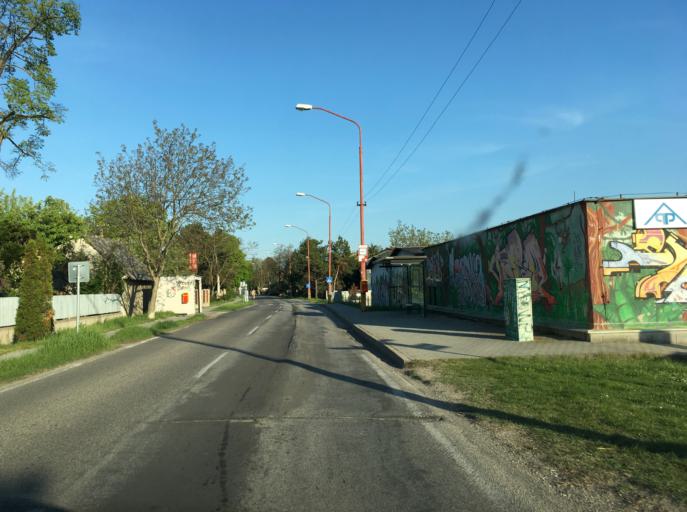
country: AT
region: Burgenland
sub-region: Politischer Bezirk Neusiedl am See
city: Deutsch Jahrndorf
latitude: 48.0580
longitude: 17.1382
